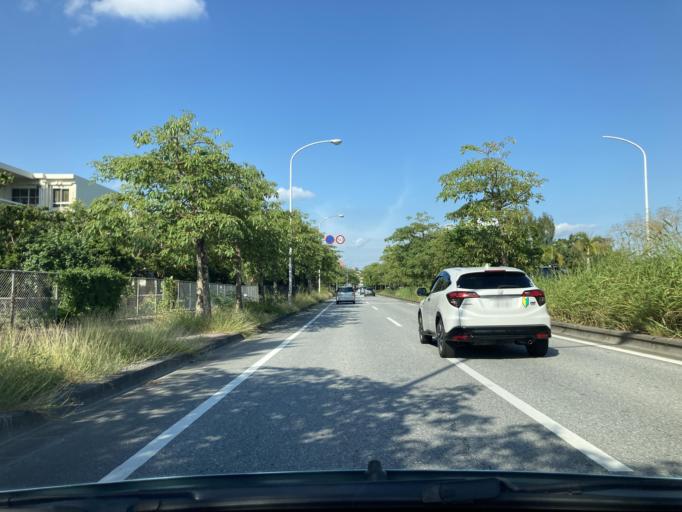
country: JP
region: Okinawa
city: Okinawa
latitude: 26.3037
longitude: 127.8151
